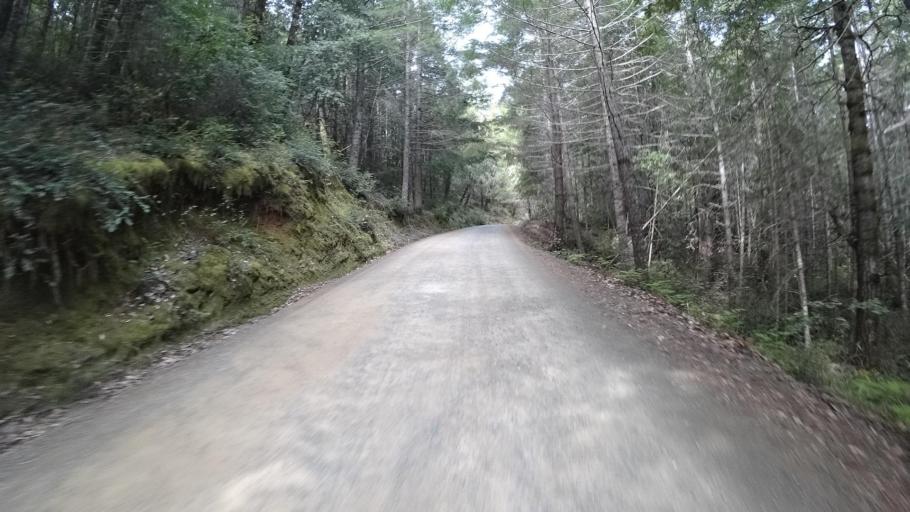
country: US
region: California
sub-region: Humboldt County
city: Redway
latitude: 40.0428
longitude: -123.8449
